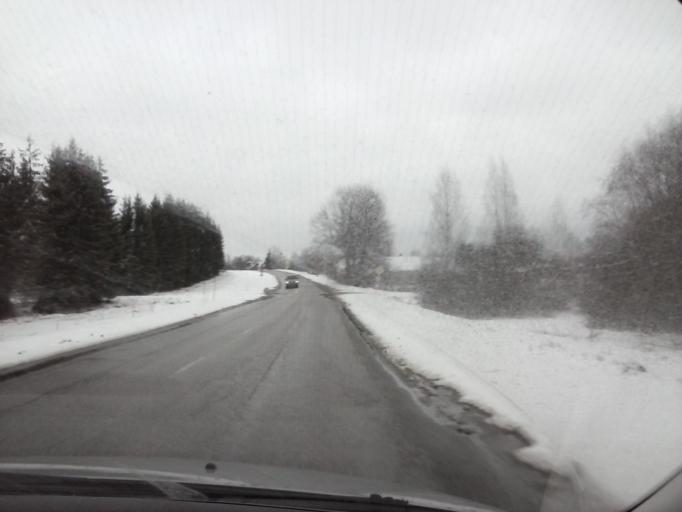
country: LV
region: Valkas Rajons
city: Valka
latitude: 57.7627
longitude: 26.0004
